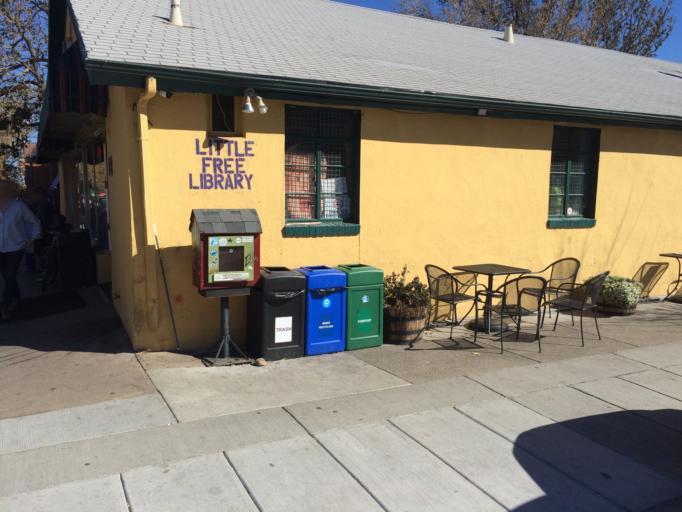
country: US
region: Colorado
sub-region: Boulder County
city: Boulder
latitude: 40.0167
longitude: -105.2851
